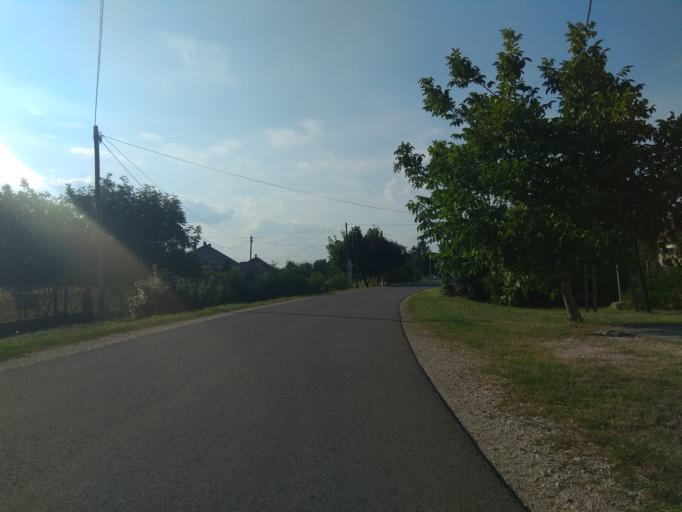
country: HU
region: Borsod-Abauj-Zemplen
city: Emod
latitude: 47.8892
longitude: 20.7649
